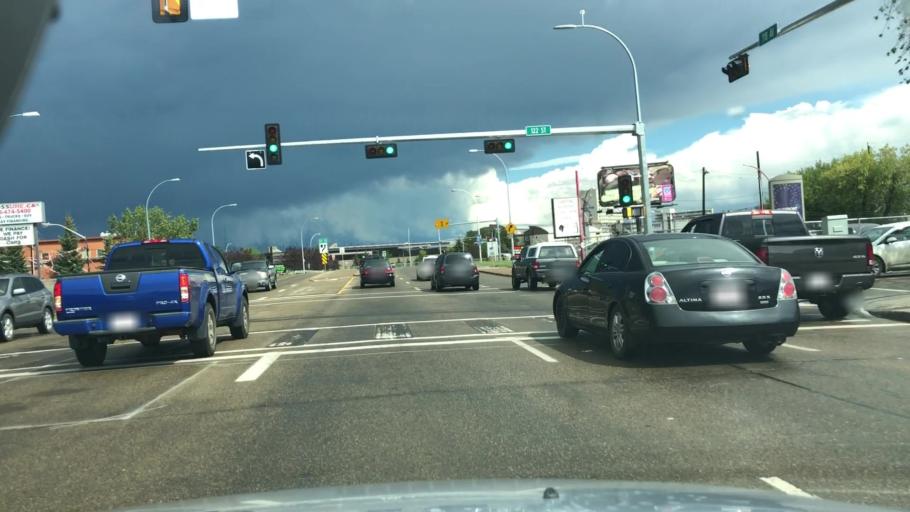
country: CA
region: Alberta
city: Edmonton
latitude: 53.5703
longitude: -113.5328
